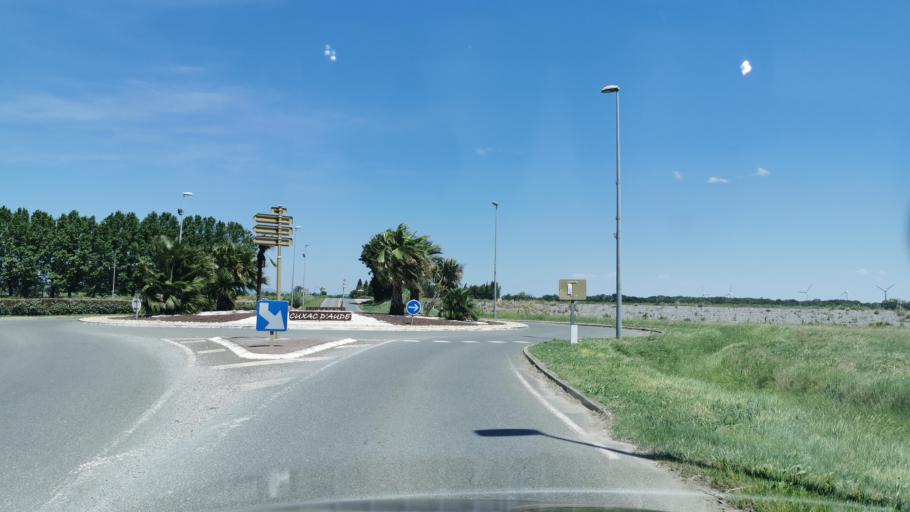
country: FR
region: Languedoc-Roussillon
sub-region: Departement de l'Aude
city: Ouveillan
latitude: 43.2507
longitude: 3.0029
